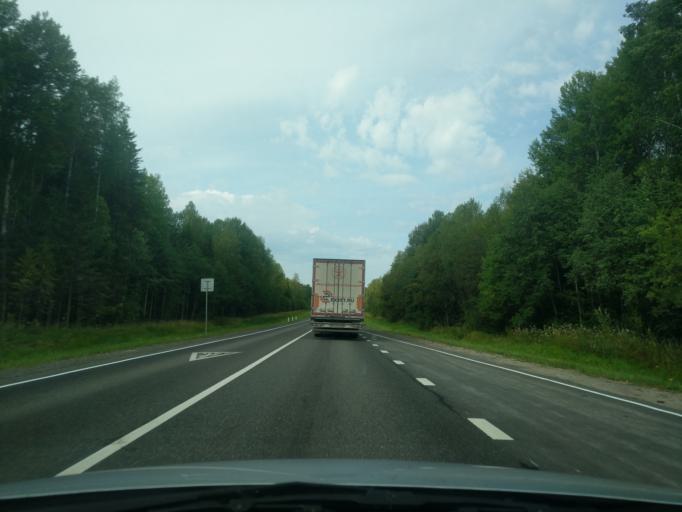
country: RU
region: Kirov
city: Leninskoye
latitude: 58.3190
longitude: 46.8645
